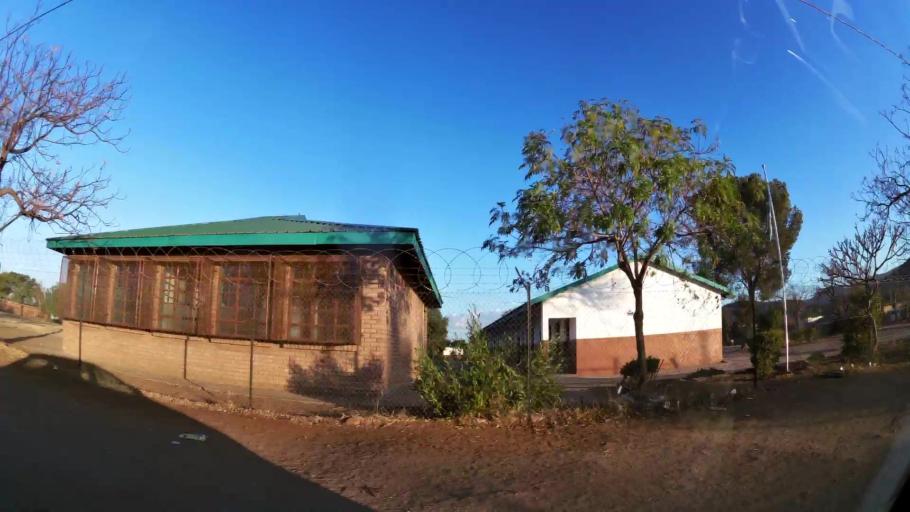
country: ZA
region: Limpopo
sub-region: Waterberg District Municipality
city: Mokopane
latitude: -24.1416
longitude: 28.9775
